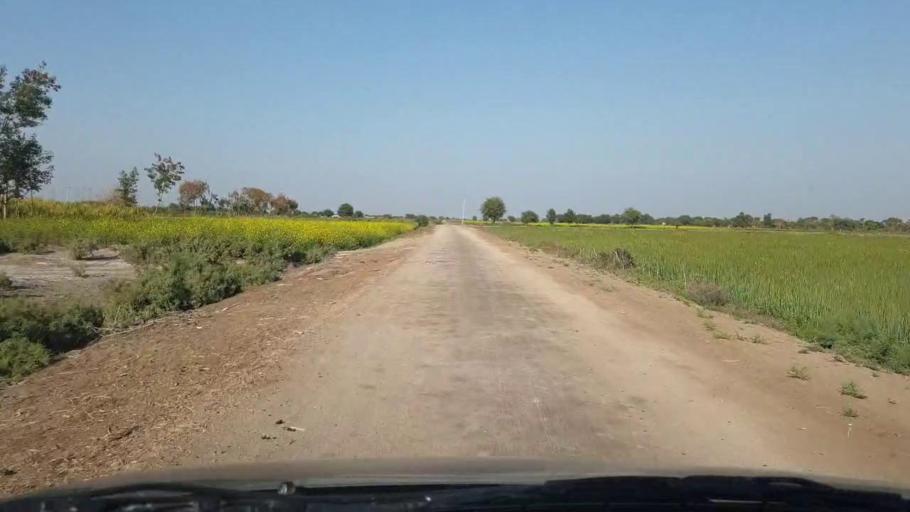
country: PK
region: Sindh
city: Digri
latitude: 25.1445
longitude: 69.2834
